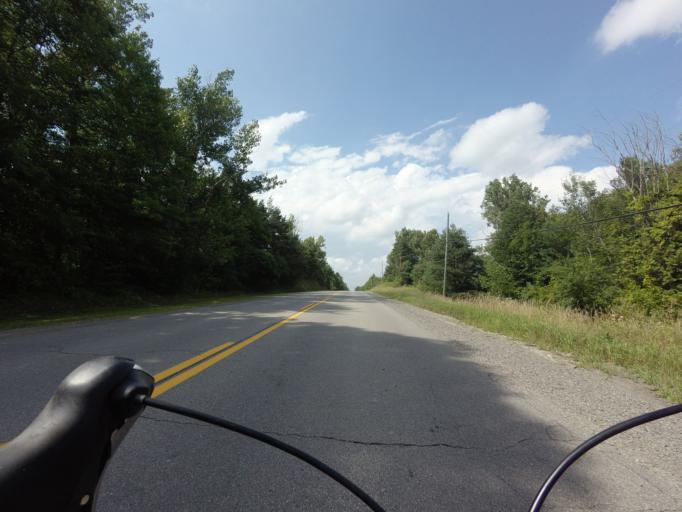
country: CA
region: Ontario
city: Brockville
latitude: 44.6757
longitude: -75.7301
